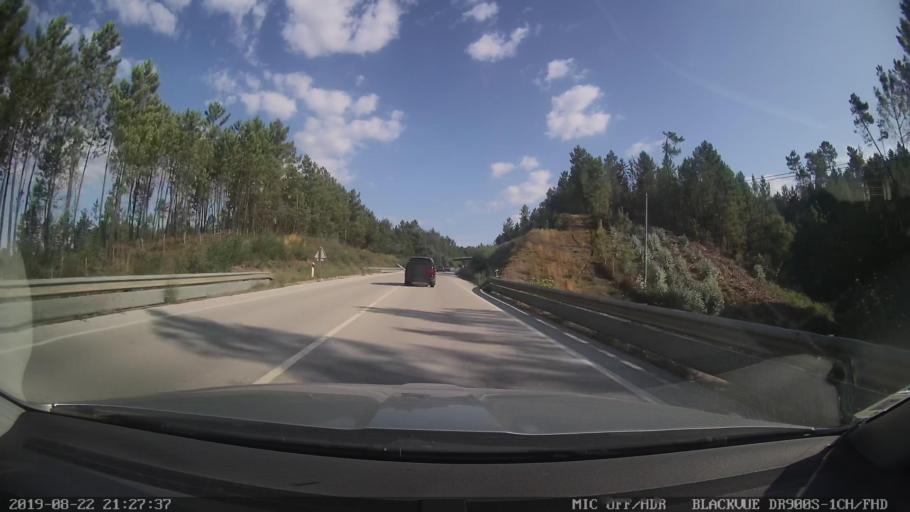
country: PT
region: Leiria
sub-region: Pedrogao Grande
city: Pedrogao Grande
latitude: 39.8810
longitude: -8.1195
